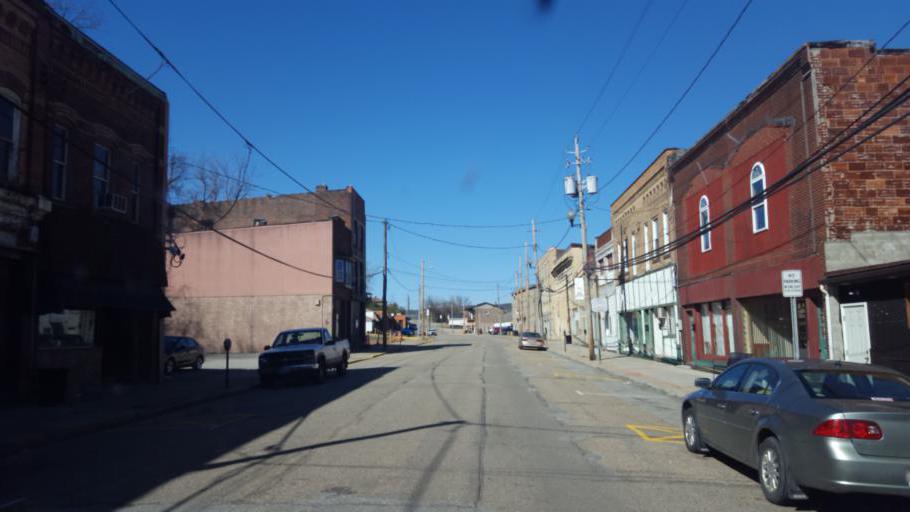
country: US
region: Ohio
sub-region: Jefferson County
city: Mingo Junction
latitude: 40.3205
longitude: -80.6066
